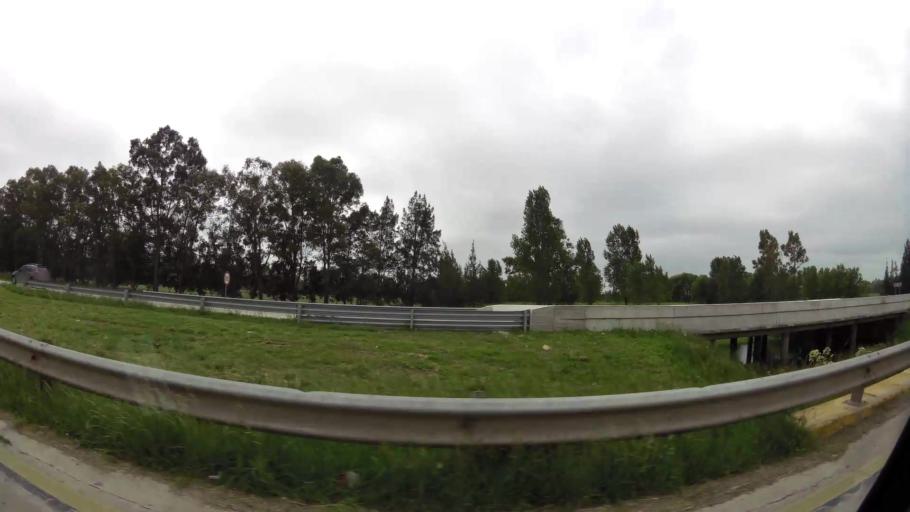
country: AR
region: Buenos Aires
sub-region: Partido de Brandsen
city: Brandsen
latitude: -35.0257
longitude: -58.2249
